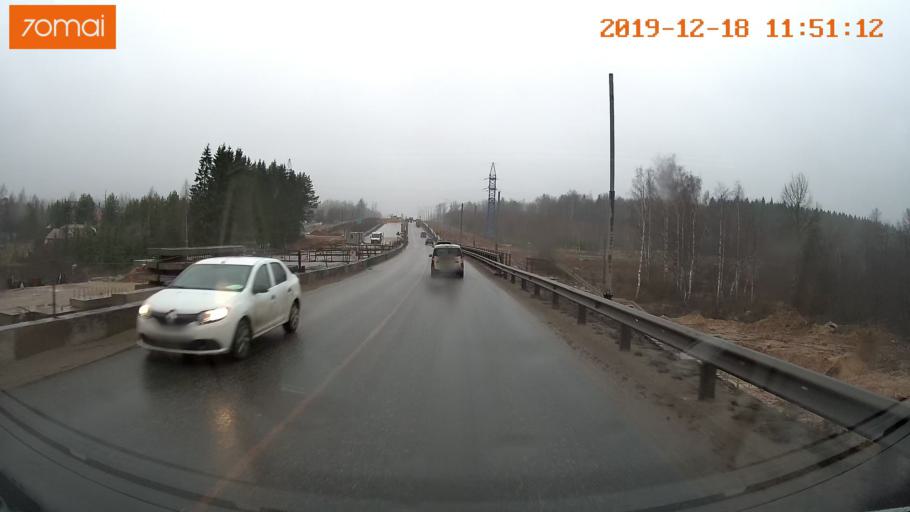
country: RU
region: Moskovskaya
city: Yershovo
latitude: 55.7918
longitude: 36.9219
